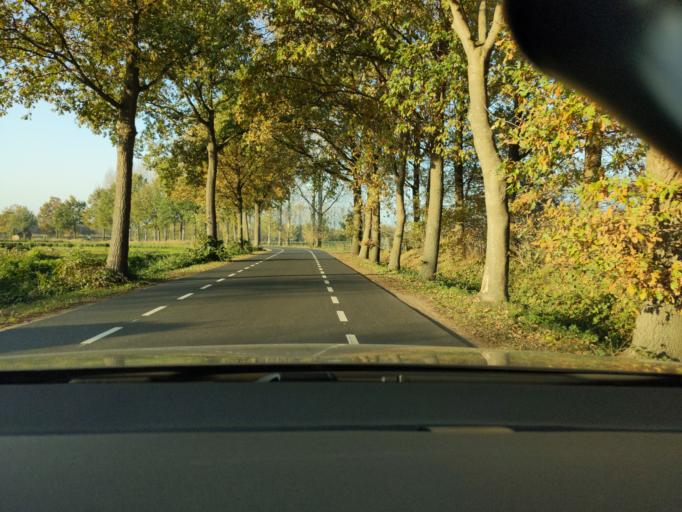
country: NL
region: North Brabant
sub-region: Gemeente Sint-Oedenrode
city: Sint-Oedenrode
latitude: 51.5612
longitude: 5.4254
